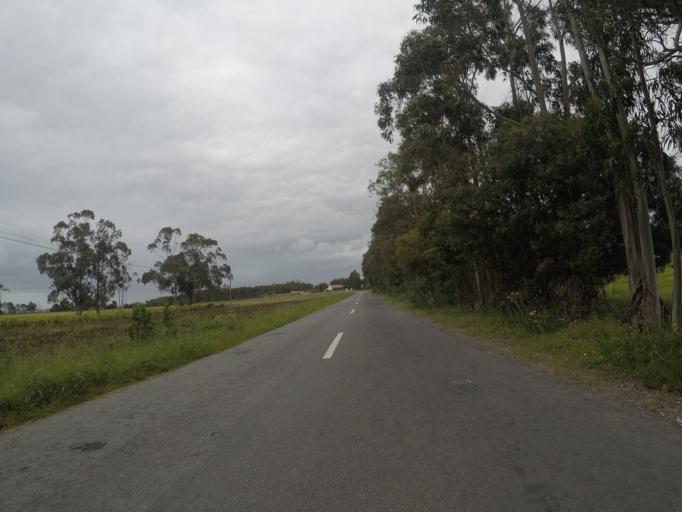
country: PT
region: Beja
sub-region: Odemira
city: Sao Teotonio
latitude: 37.5895
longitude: -8.7778
